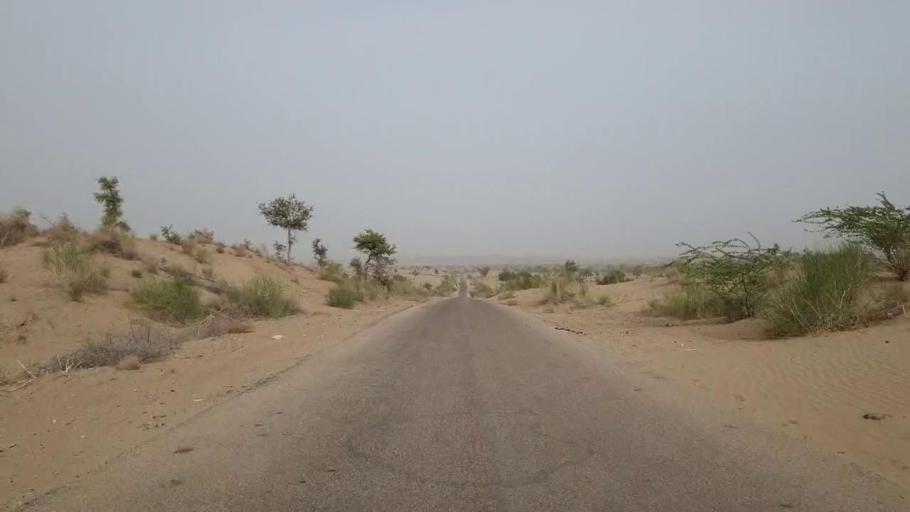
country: PK
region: Sindh
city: Islamkot
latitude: 24.5552
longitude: 70.3491
